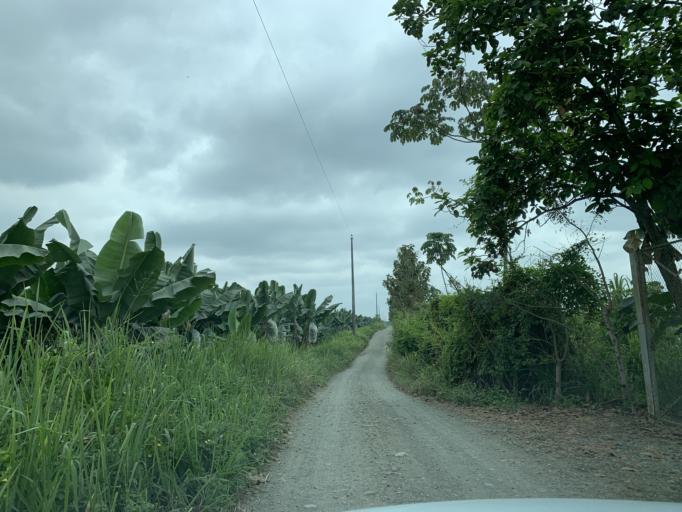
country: EC
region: Guayas
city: Coronel Marcelino Mariduena
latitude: -2.3401
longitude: -79.4572
